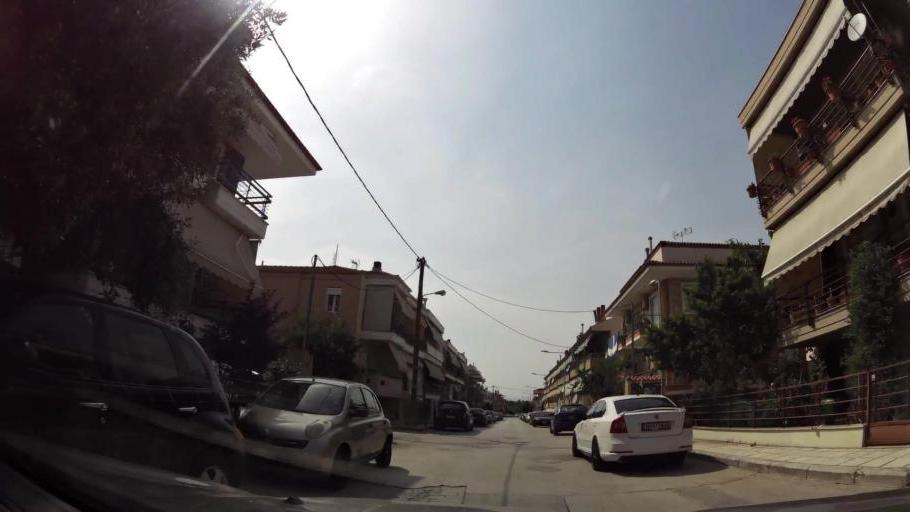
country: GR
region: Central Macedonia
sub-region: Nomos Thessalonikis
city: Efkarpia
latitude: 40.6834
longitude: 22.9487
